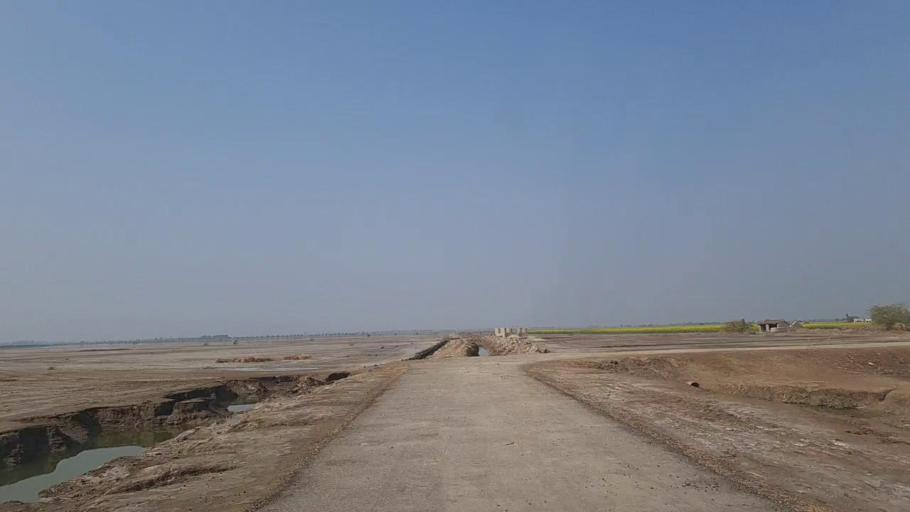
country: PK
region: Sindh
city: Nawabshah
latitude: 26.3468
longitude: 68.4536
